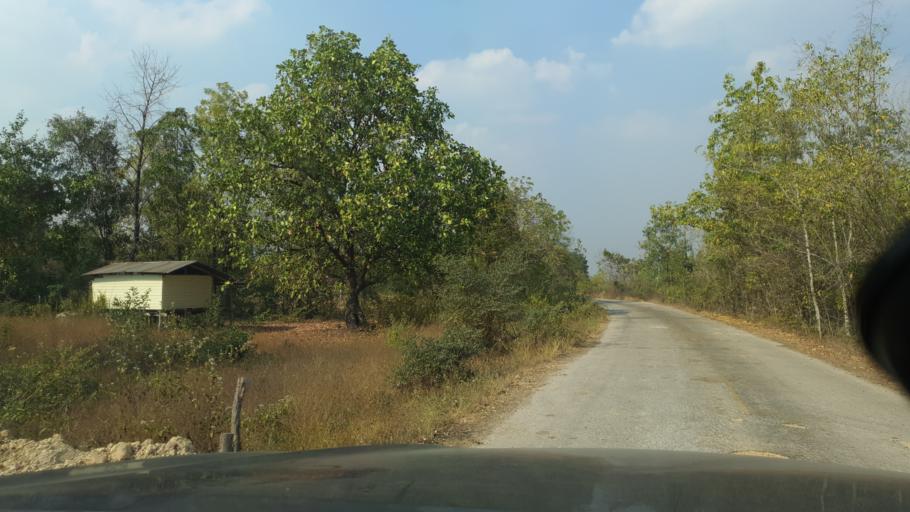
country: TH
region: Sukhothai
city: Ban Dan Lan Hoi
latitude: 17.0143
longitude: 99.5583
